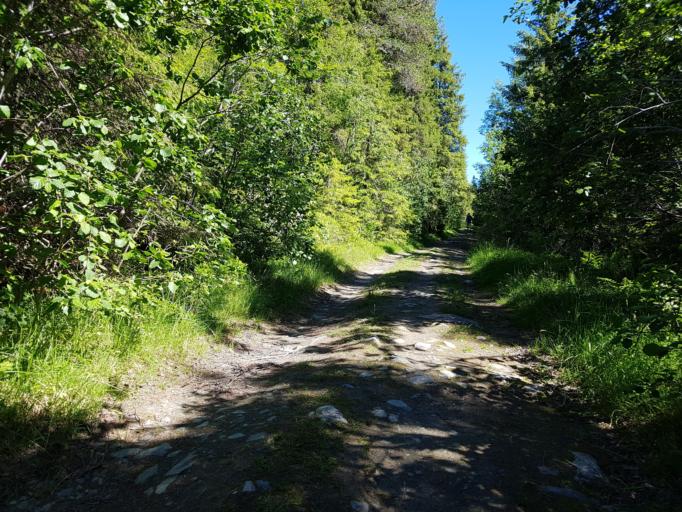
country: NO
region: Sor-Trondelag
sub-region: Melhus
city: Melhus
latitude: 63.4312
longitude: 10.2177
